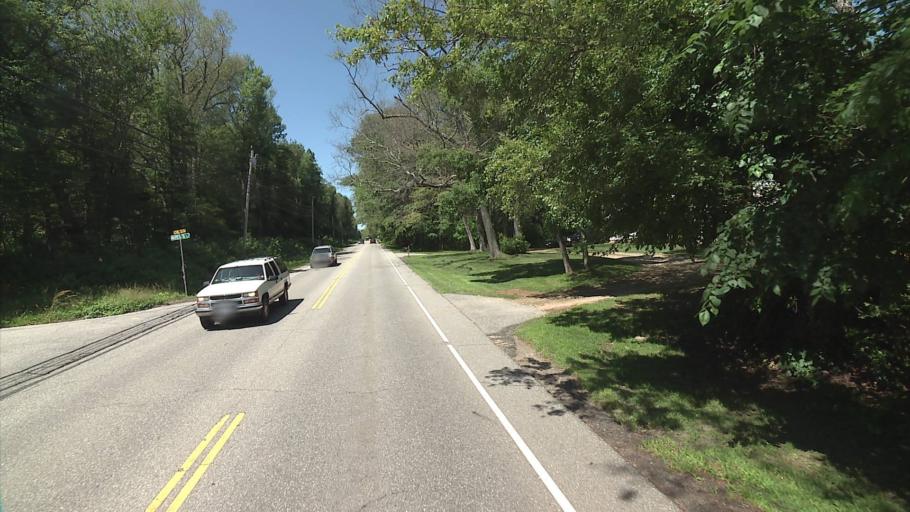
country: US
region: Connecticut
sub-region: New London County
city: Colchester
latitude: 41.5577
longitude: -72.3710
